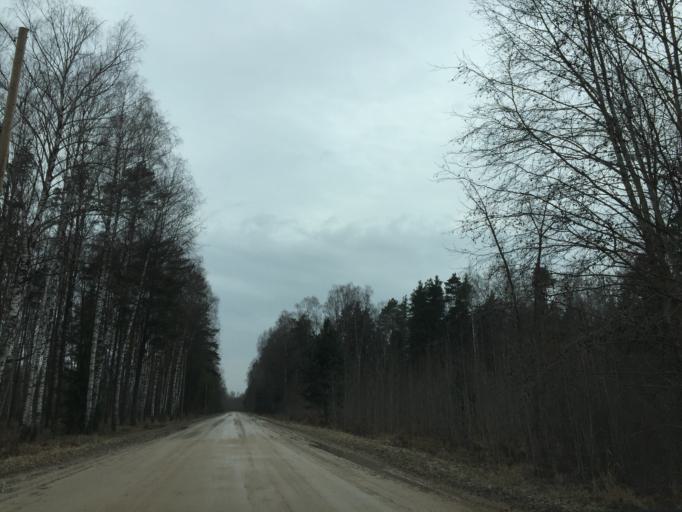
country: LV
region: Ozolnieku
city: Ozolnieki
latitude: 56.7008
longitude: 23.7392
